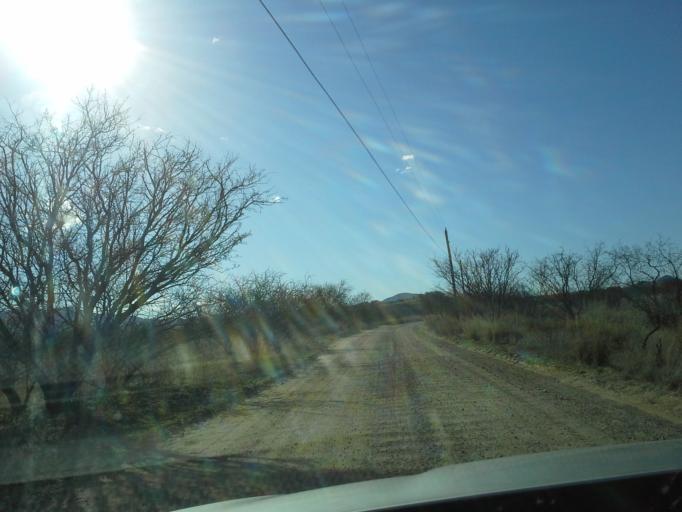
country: US
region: Arizona
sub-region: Pima County
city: Corona de Tucson
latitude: 31.7382
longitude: -110.6822
